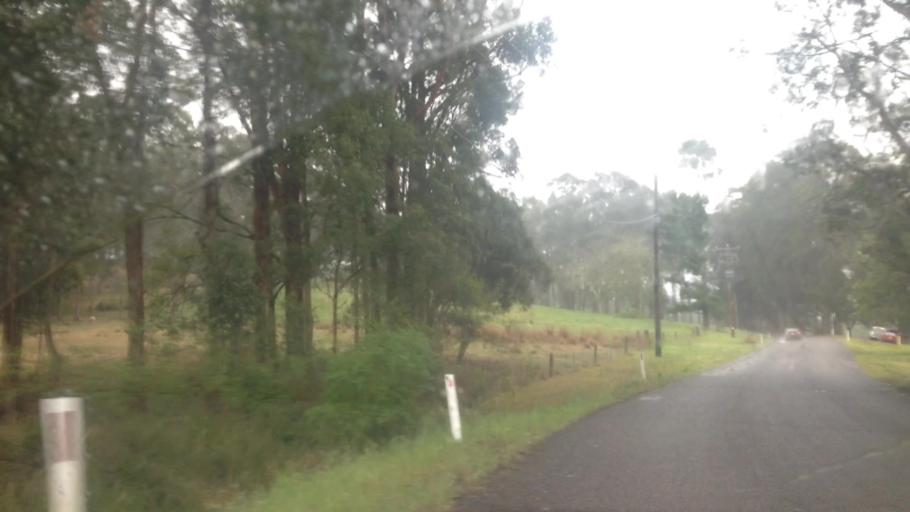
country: AU
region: New South Wales
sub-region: Wyong Shire
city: Little Jilliby
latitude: -33.2109
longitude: 151.3702
